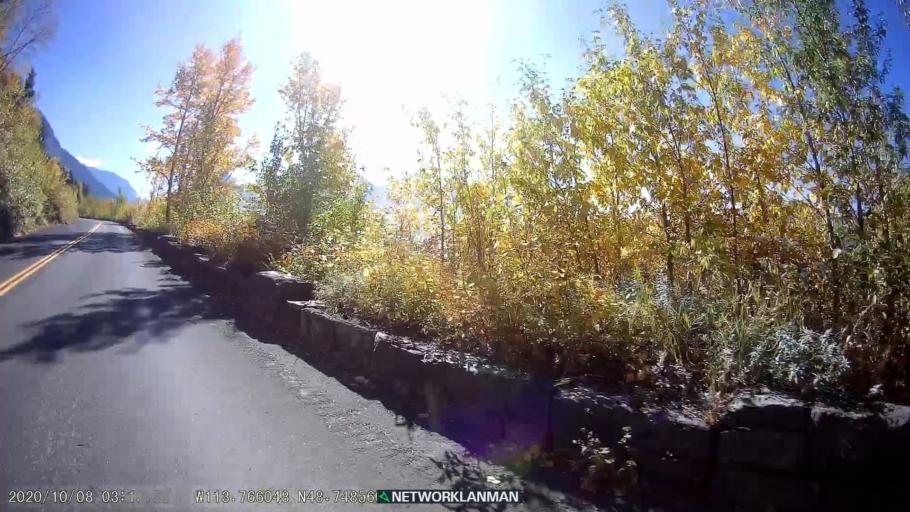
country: US
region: Montana
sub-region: Flathead County
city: Columbia Falls
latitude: 48.7485
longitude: -113.7657
